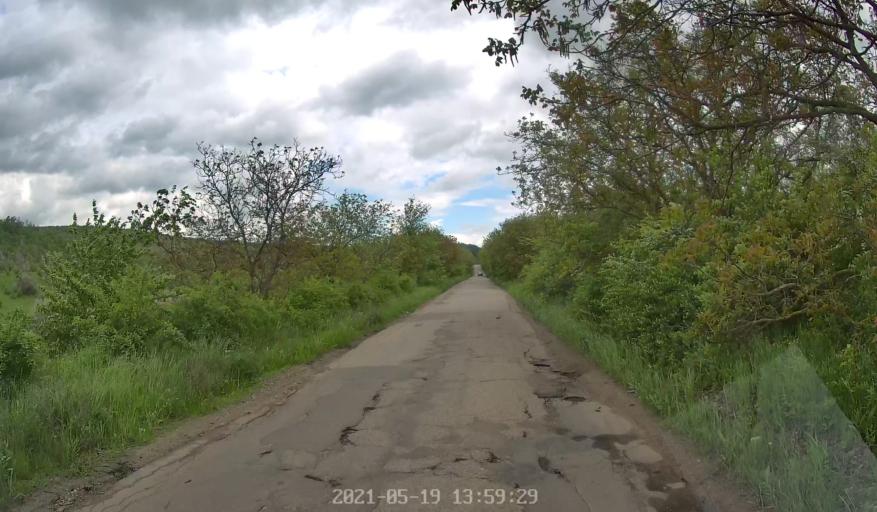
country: MD
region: Chisinau
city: Chisinau
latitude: 47.0400
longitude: 28.9241
